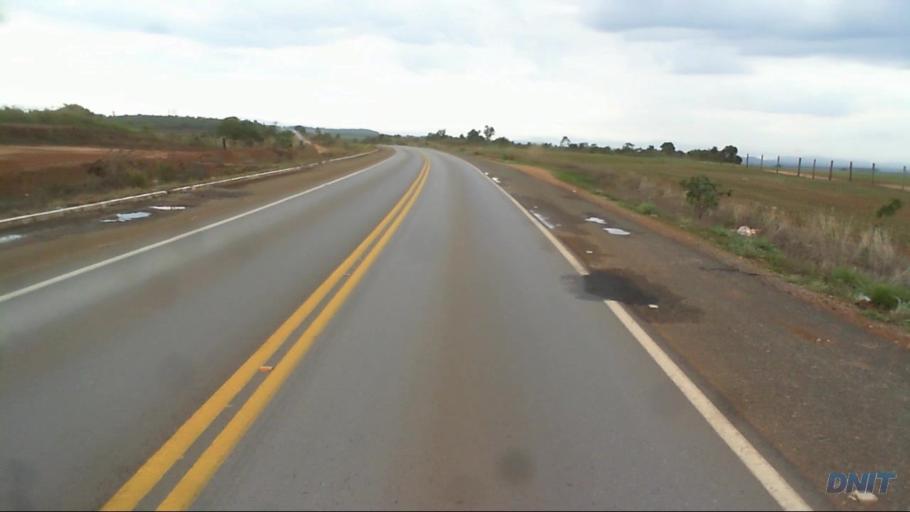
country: BR
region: Goias
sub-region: Uruacu
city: Uruacu
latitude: -14.6527
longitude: -49.1614
